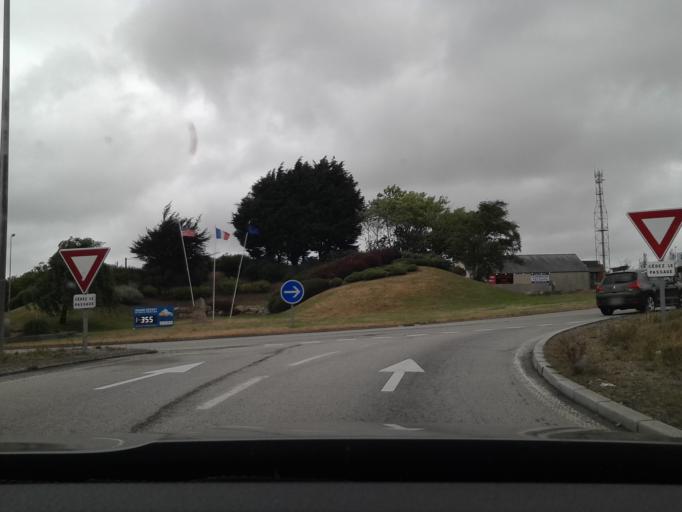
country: FR
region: Lower Normandy
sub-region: Departement de la Manche
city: La Glacerie
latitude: 49.5991
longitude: -1.5971
